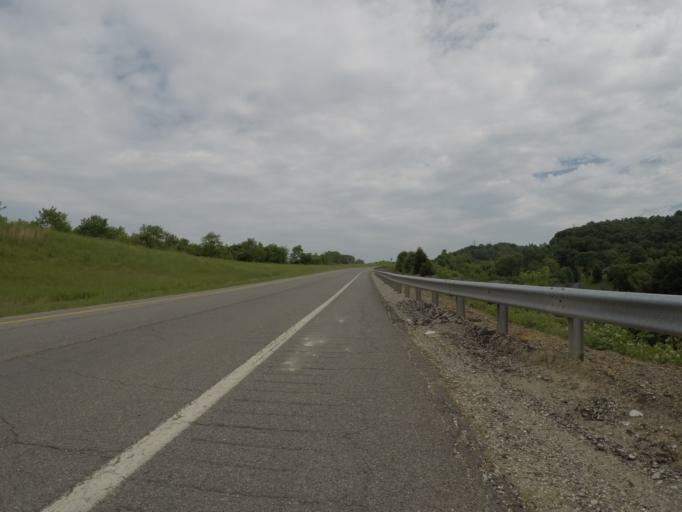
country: US
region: West Virginia
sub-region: Wayne County
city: Kenova
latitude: 38.3714
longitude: -82.5881
